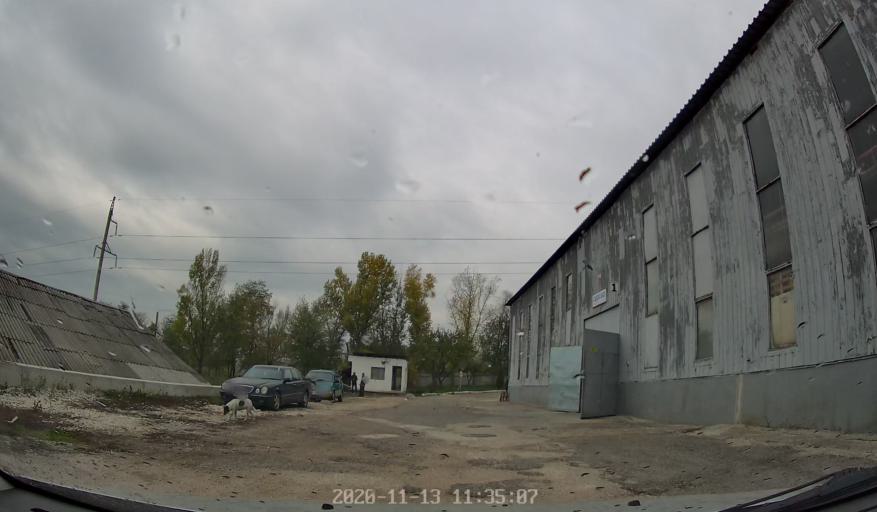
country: MD
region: Chisinau
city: Chisinau
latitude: 46.9863
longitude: 28.9156
